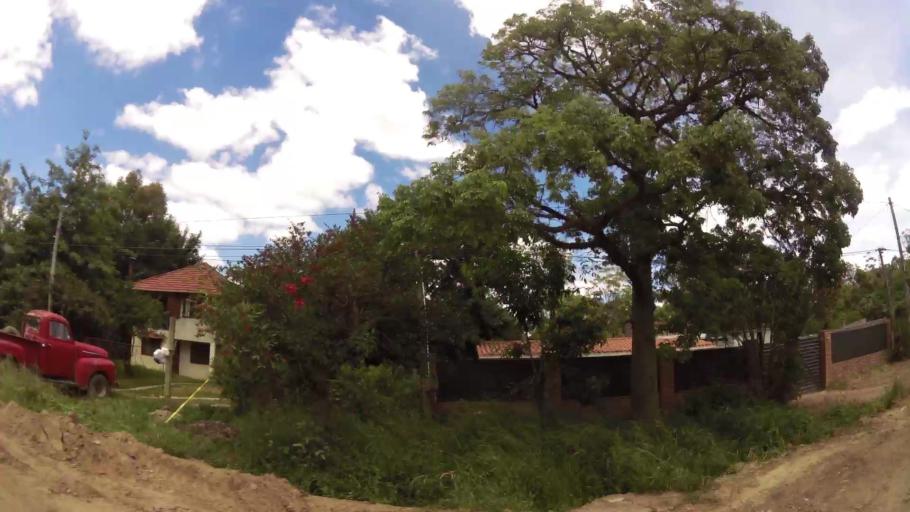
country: UY
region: Canelones
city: Colonia Nicolich
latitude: -34.8263
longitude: -55.9858
